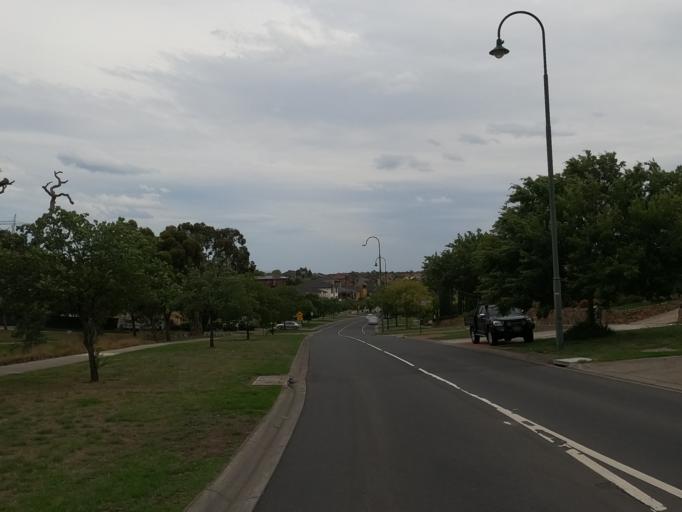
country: AU
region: Victoria
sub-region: Hume
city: Meadow Heights
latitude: -37.6408
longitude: 144.9085
